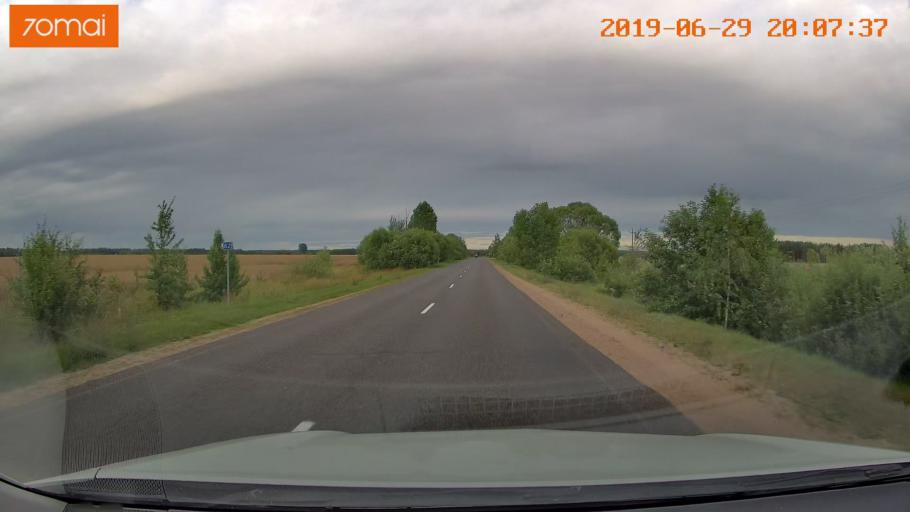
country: BY
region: Brest
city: Lahishyn
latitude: 52.3415
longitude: 26.0401
